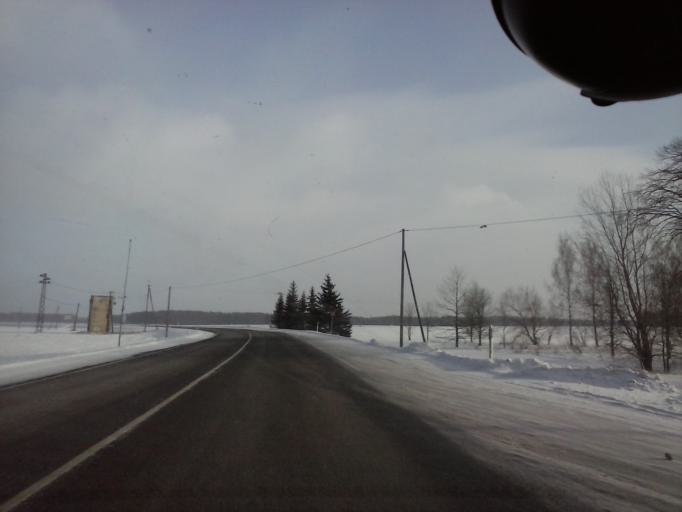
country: EE
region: Tartu
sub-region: Puhja vald
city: Puhja
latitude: 58.3314
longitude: 26.1877
